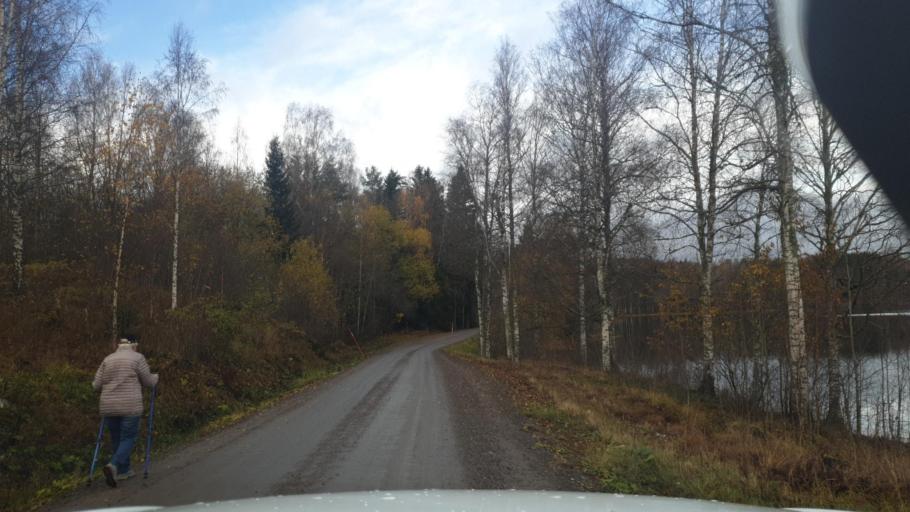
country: NO
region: Hedmark
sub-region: Eidskog
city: Skotterud
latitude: 59.8709
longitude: 11.9819
